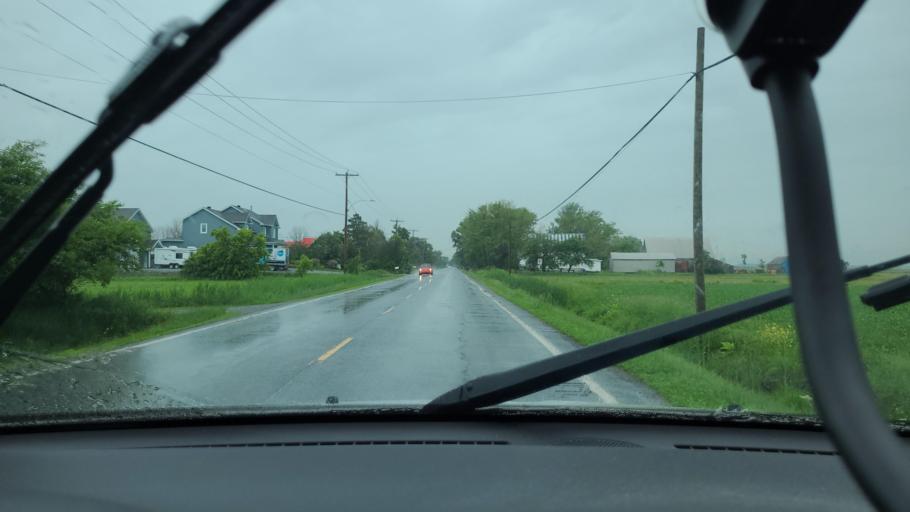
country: CA
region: Quebec
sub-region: Monteregie
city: Saint-Hyacinthe
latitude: 45.6163
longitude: -73.0339
